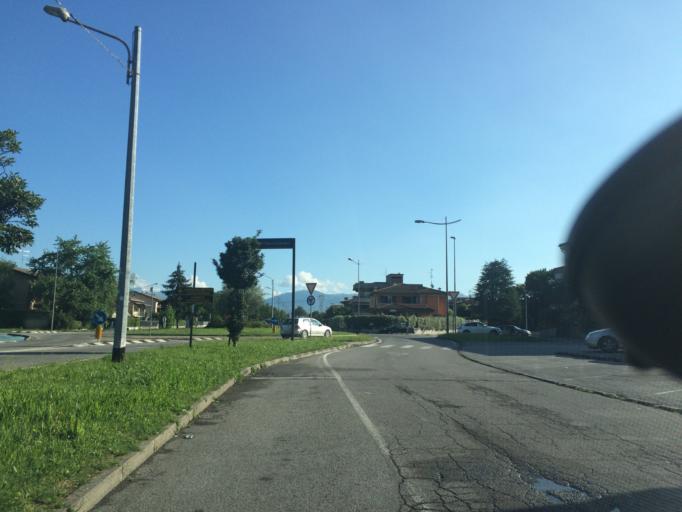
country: IT
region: Lombardy
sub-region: Provincia di Brescia
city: Flero
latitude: 45.4880
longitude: 10.1810
